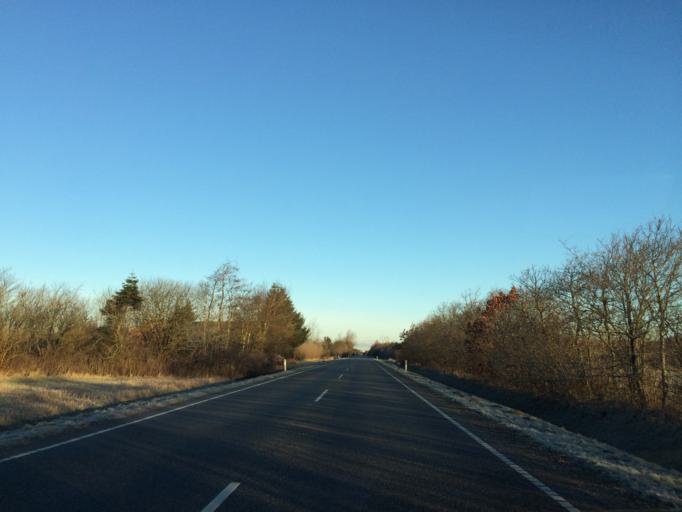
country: DK
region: Central Jutland
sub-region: Holstebro Kommune
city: Ulfborg
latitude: 56.3729
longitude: 8.3316
